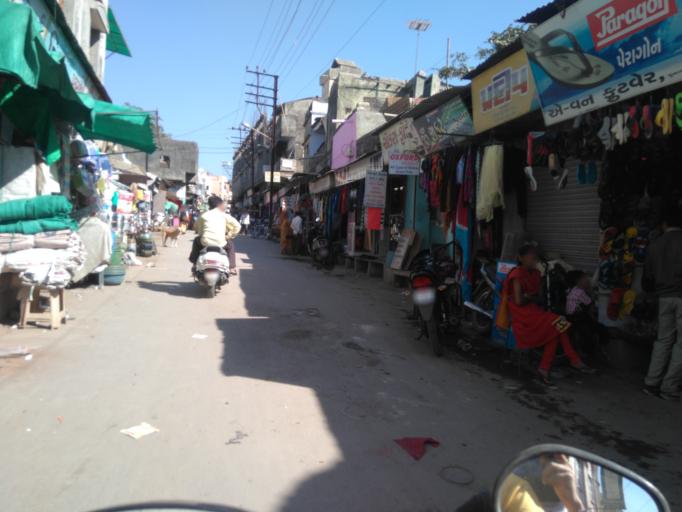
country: IN
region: Gujarat
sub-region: Junagadh
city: Junagadh
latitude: 21.5224
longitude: 70.4608
